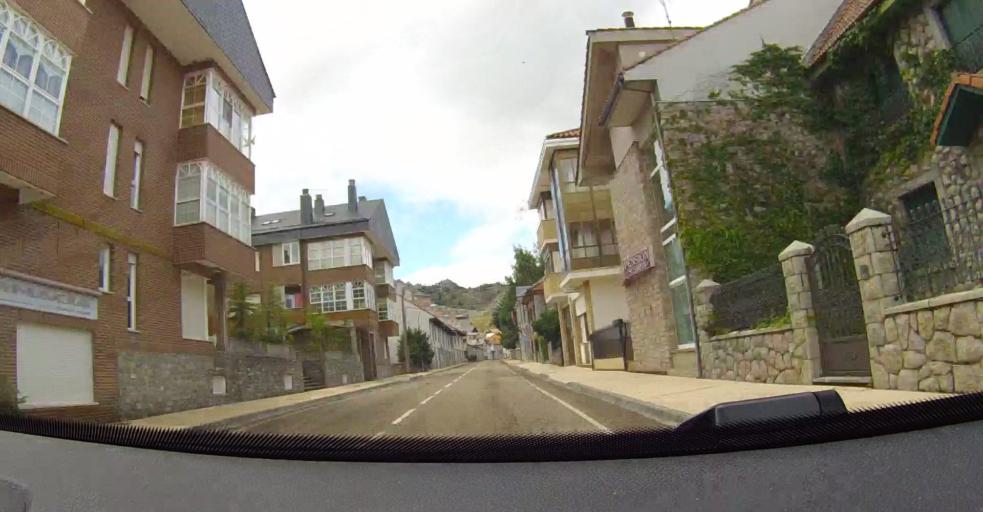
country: ES
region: Castille and Leon
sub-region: Provincia de Leon
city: Puebla de Lillo
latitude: 43.0059
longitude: -5.2721
